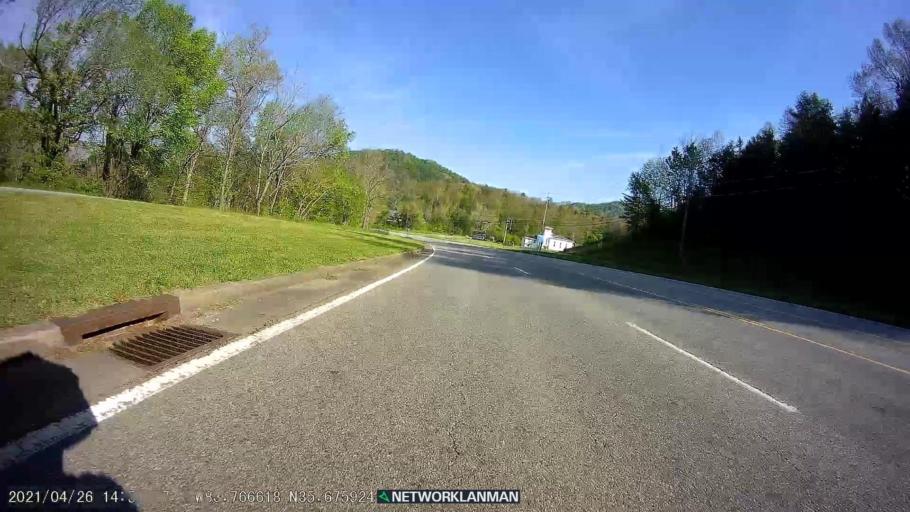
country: US
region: Tennessee
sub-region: Blount County
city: Wildwood
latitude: 35.6763
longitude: -83.7662
